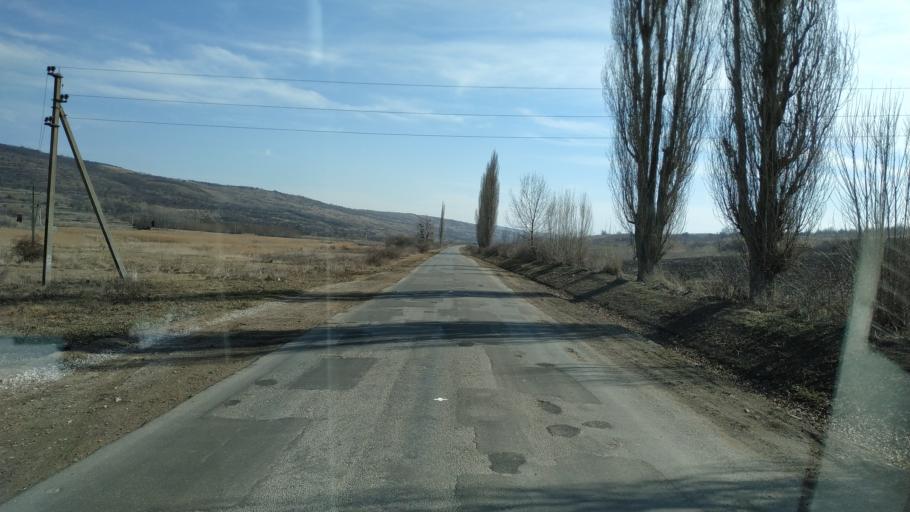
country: MD
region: Nisporeni
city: Nisporeni
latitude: 47.1698
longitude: 28.0937
